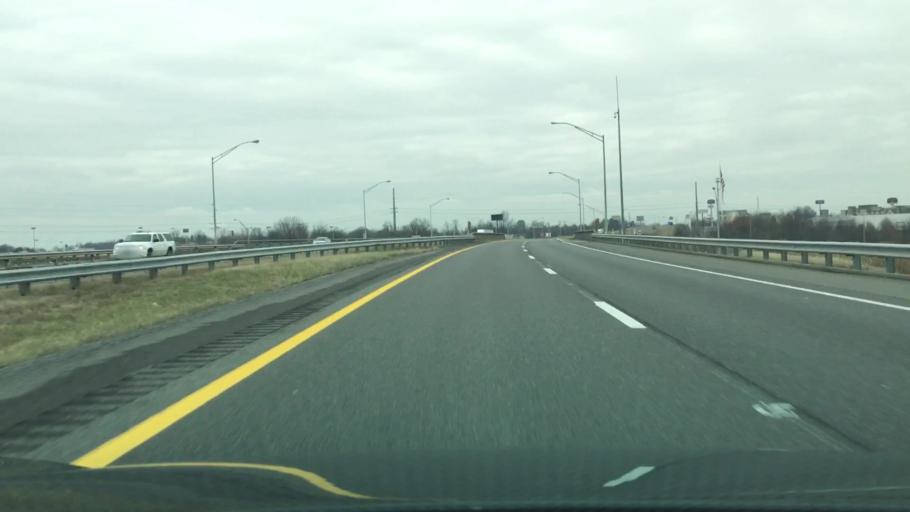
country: US
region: Kentucky
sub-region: McCracken County
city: Hendron
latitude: 37.0752
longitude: -88.6809
